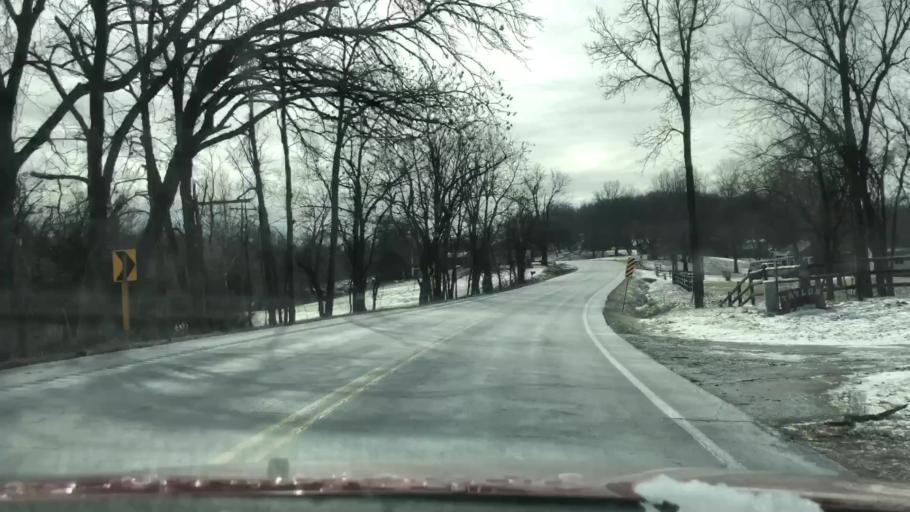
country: US
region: Missouri
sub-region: Jackson County
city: Oak Grove
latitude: 38.9413
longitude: -94.1322
